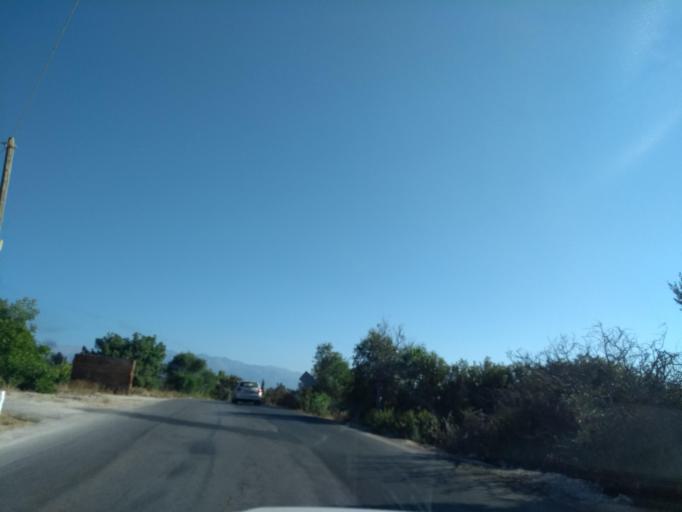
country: GR
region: Crete
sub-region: Nomos Chanias
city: Pithari
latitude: 35.5600
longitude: 24.0906
